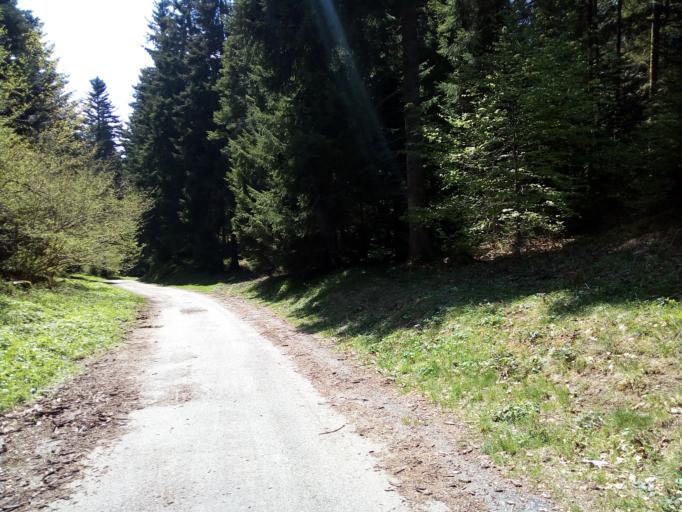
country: FR
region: Rhone-Alpes
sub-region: Departement de l'Isere
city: Revel
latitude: 45.1451
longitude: 5.8694
